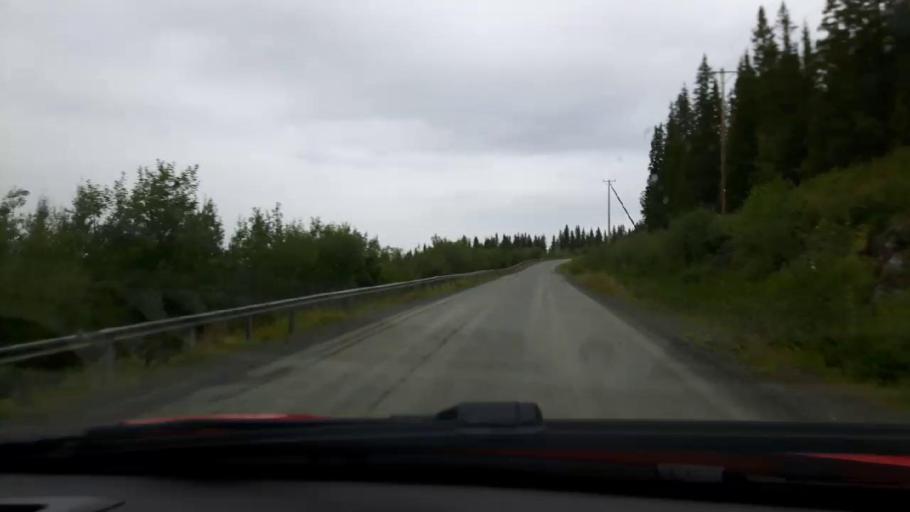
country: SE
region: Jaemtland
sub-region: Are Kommun
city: Are
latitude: 63.4034
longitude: 12.8368
